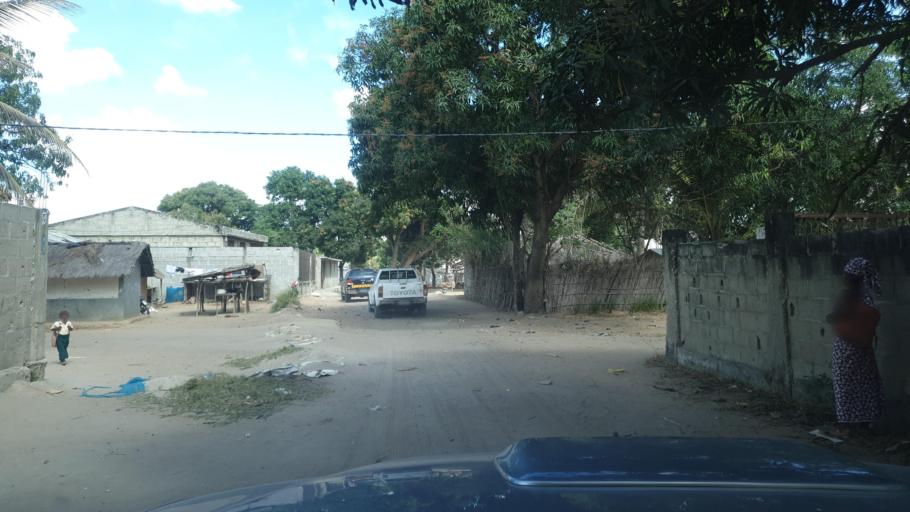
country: MZ
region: Nampula
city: Nacala
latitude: -14.5688
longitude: 40.7001
